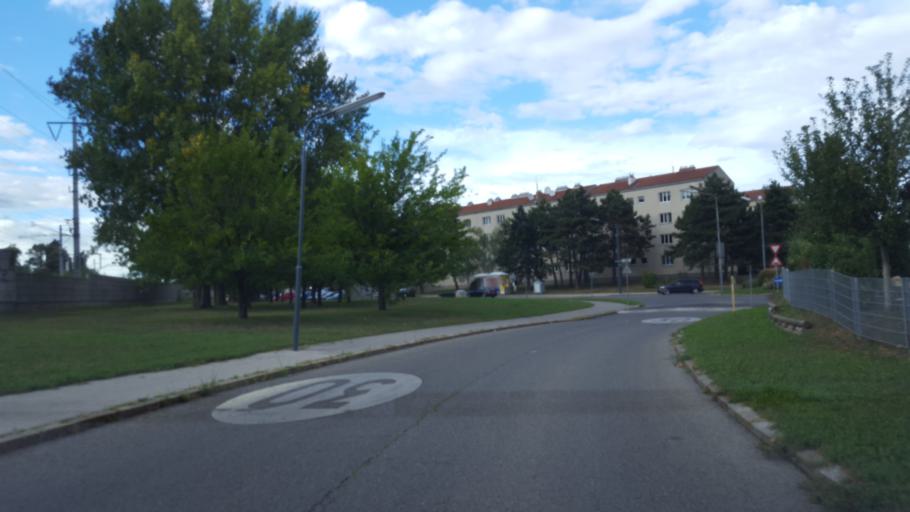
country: AT
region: Lower Austria
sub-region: Politischer Bezirk Wien-Umgebung
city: Schwechat
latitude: 48.1573
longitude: 16.4243
